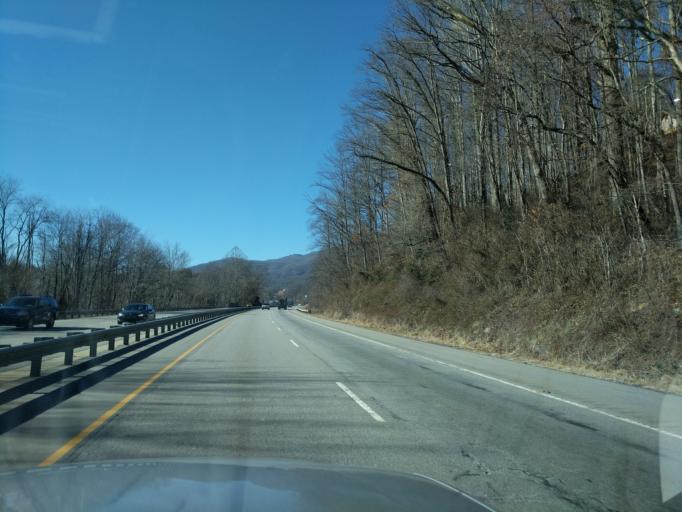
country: US
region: North Carolina
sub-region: Haywood County
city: Hazelwood
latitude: 35.4564
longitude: -83.0354
